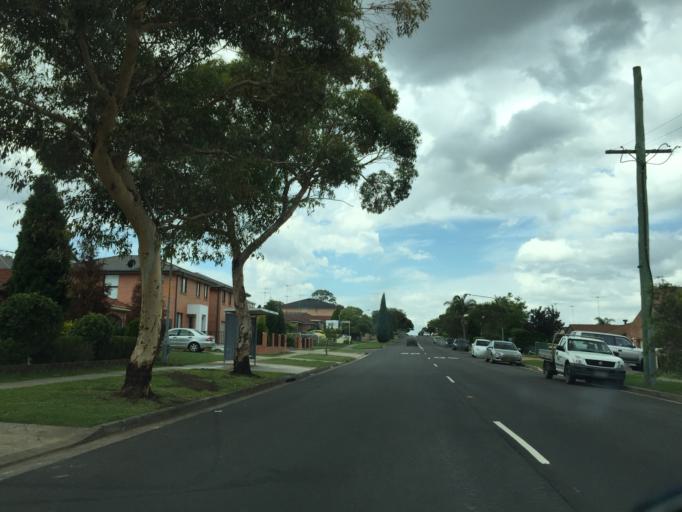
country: AU
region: New South Wales
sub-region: Blacktown
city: Doonside
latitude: -33.7804
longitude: 150.8768
